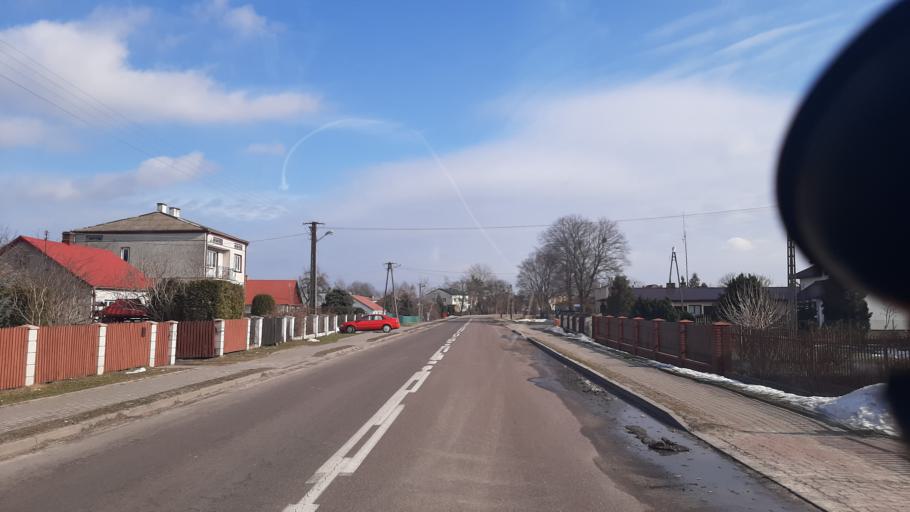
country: PL
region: Lublin Voivodeship
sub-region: Powiat wlodawski
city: Hansk
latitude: 51.4802
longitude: 23.2946
